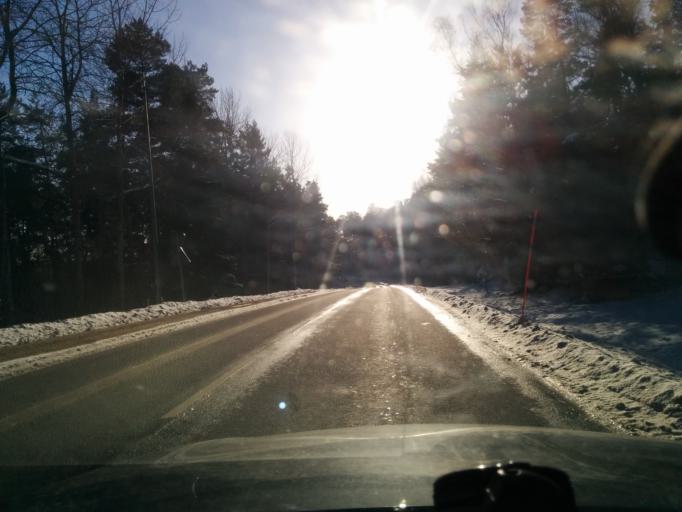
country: SE
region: Stockholm
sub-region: Taby Kommun
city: Taby
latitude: 59.4813
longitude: 18.0952
